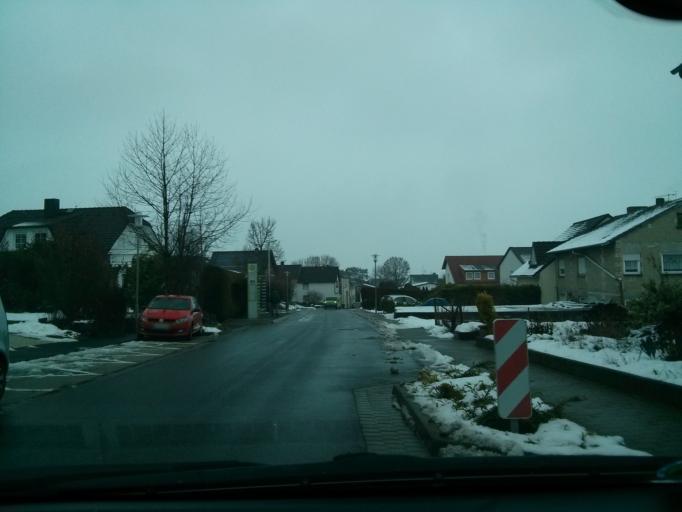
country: DE
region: North Rhine-Westphalia
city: Meckenheim
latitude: 50.5893
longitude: 7.0111
